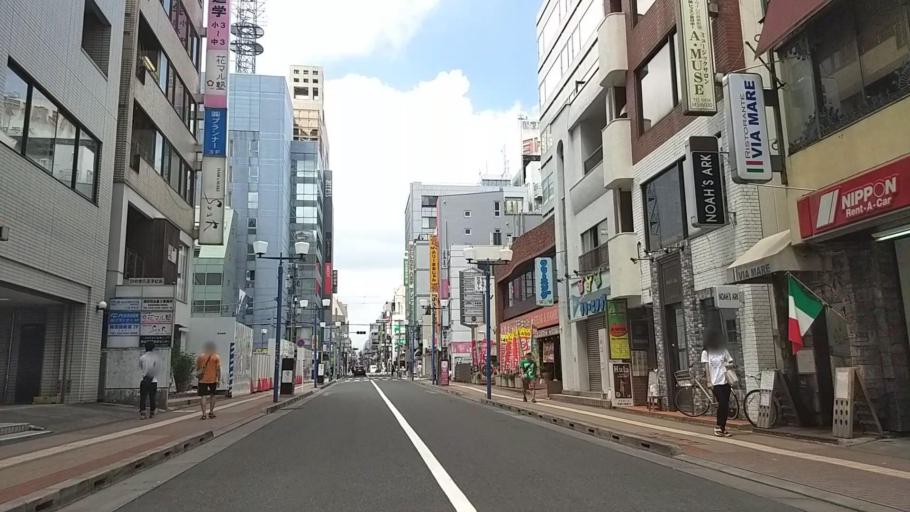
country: JP
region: Tokyo
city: Hachioji
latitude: 35.6576
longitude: 139.3411
